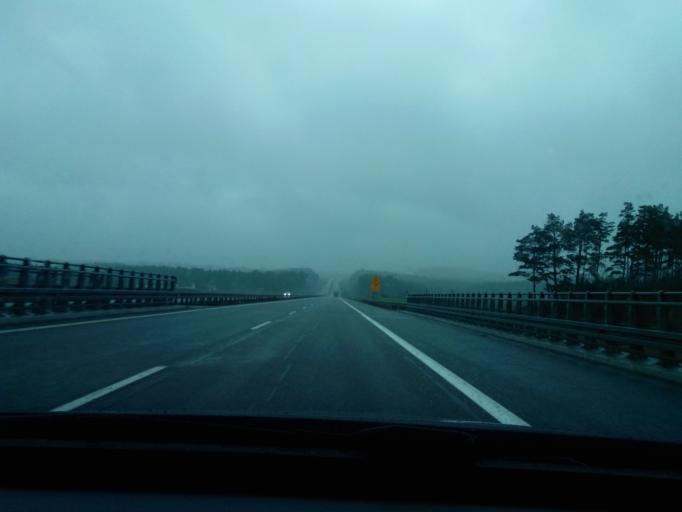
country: PL
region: Pomeranian Voivodeship
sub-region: Powiat tczewski
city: Subkowy
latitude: 54.0493
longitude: 18.6717
